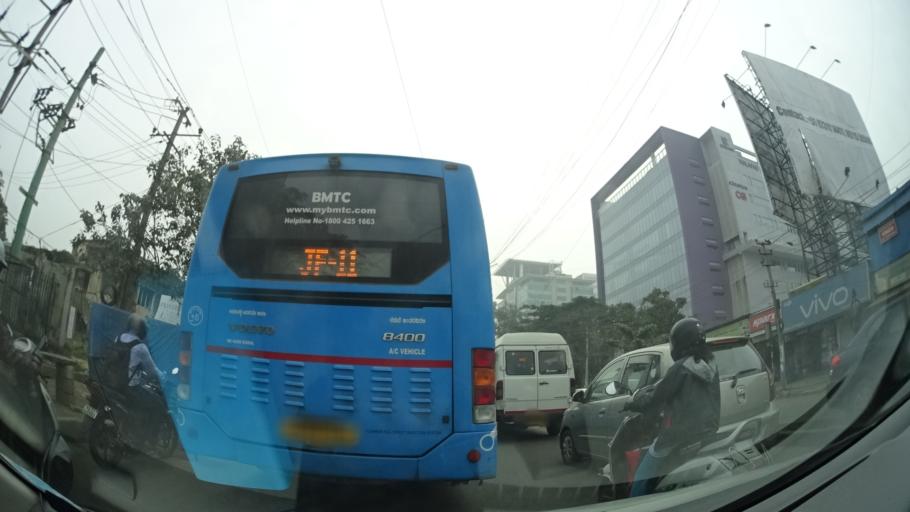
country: IN
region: Karnataka
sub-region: Bangalore Urban
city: Bangalore
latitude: 12.9939
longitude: 77.7021
